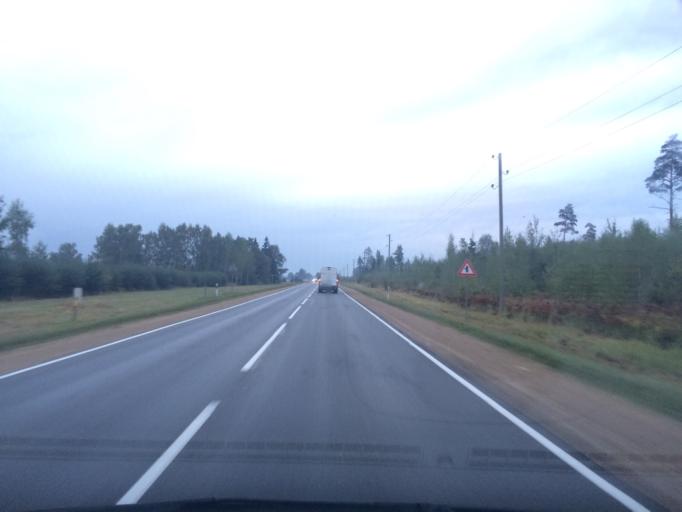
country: LV
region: Salas
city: Sala
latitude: 56.5677
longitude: 25.7753
